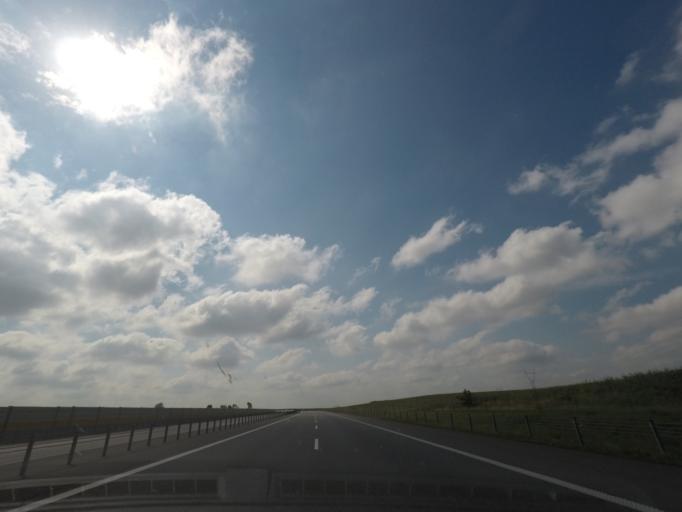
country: PL
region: Kujawsko-Pomorskie
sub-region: Powiat chelminski
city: Lisewo
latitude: 53.2285
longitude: 18.7277
